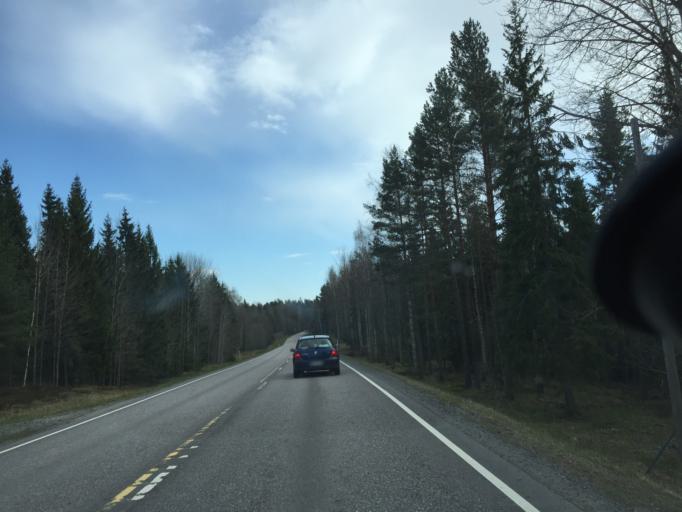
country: FI
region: Uusimaa
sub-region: Raaseporin
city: Ekenaes
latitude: 60.0262
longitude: 23.3715
